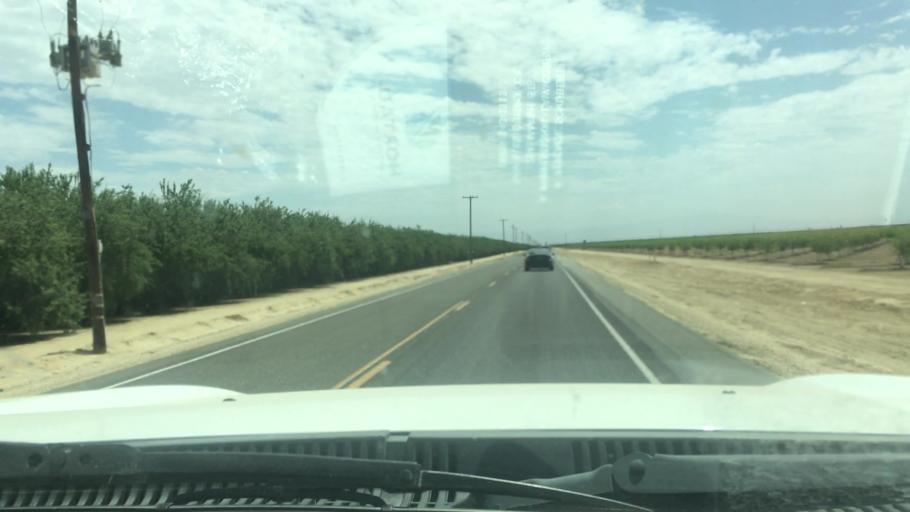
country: US
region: California
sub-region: Kern County
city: Wasco
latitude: 35.5580
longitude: -119.3121
